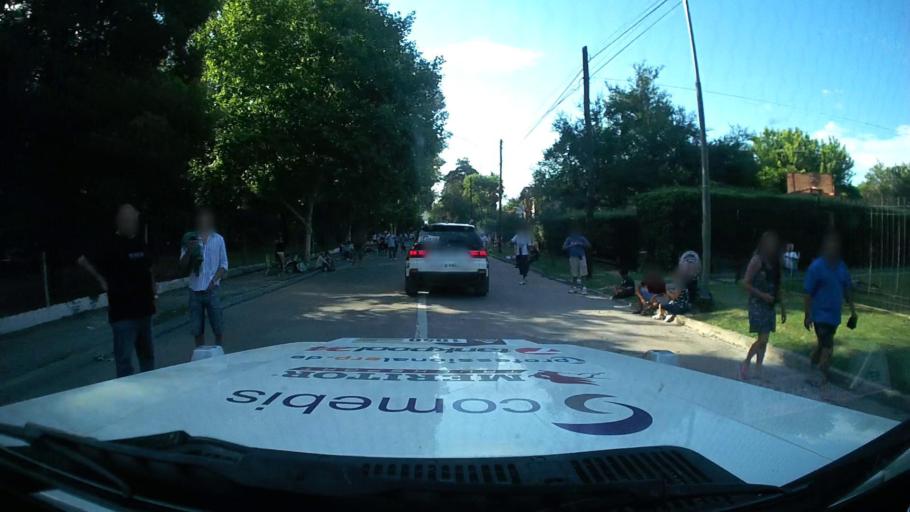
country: AR
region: Cordoba
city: Villa Carlos Paz
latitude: -31.3979
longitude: -64.4695
